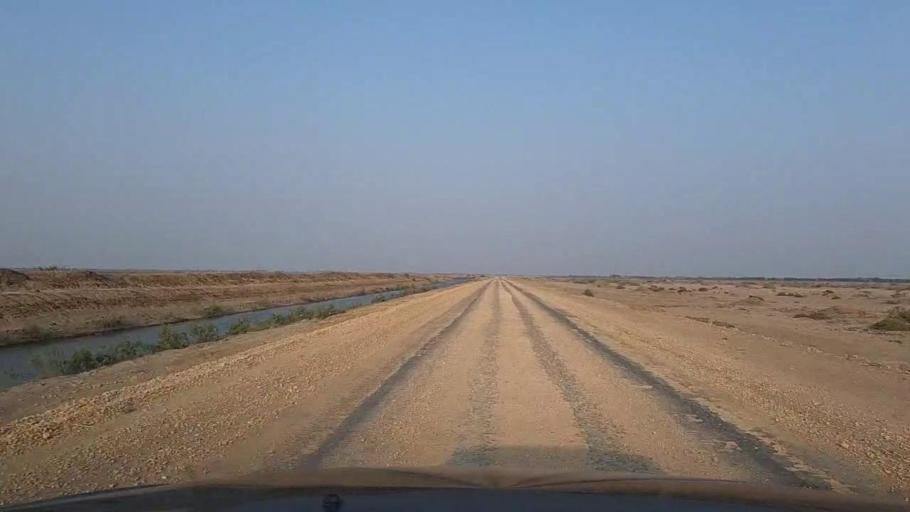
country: PK
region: Sindh
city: Mirpur Sakro
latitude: 24.4293
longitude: 67.7567
